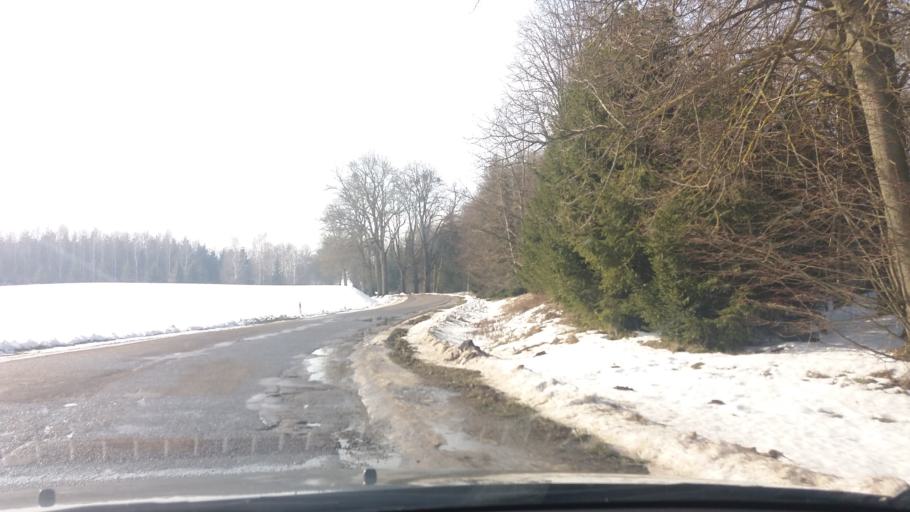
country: PL
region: Warmian-Masurian Voivodeship
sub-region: Powiat bartoszycki
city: Bisztynek
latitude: 54.1058
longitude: 20.8200
